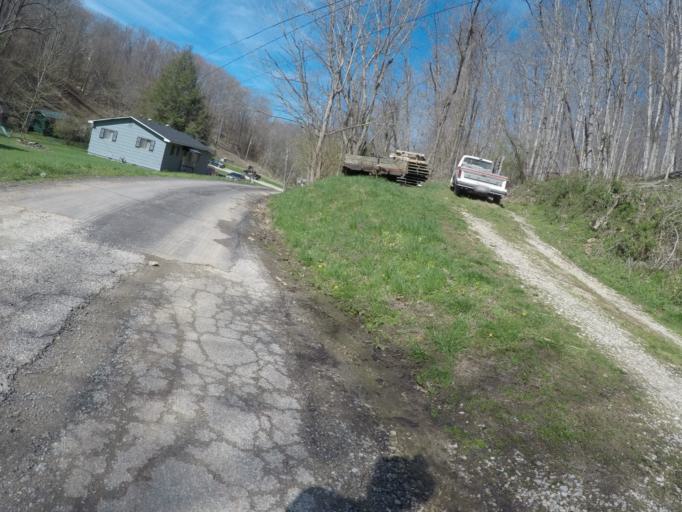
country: US
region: West Virginia
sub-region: Cabell County
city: Pea Ridge
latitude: 38.3992
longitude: -82.3468
